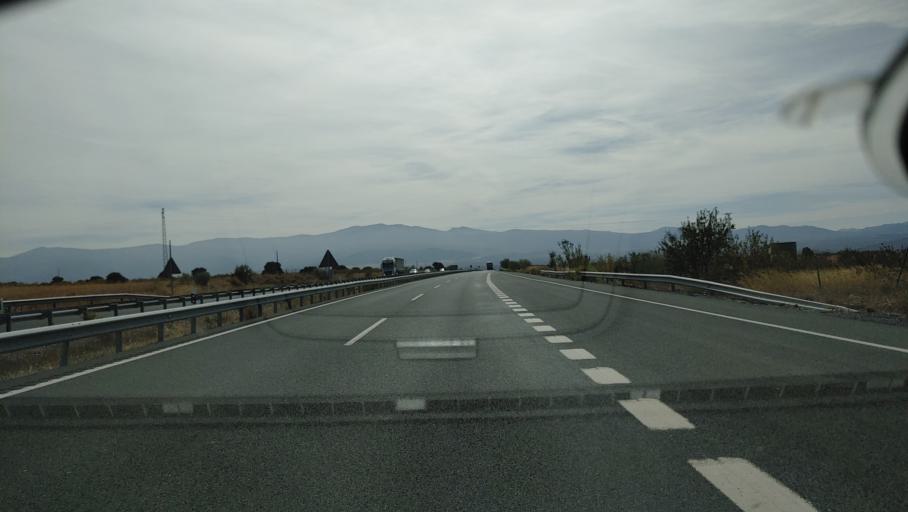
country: ES
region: Andalusia
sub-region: Provincia de Granada
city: Benalua de Guadix
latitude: 37.3657
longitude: -3.0742
